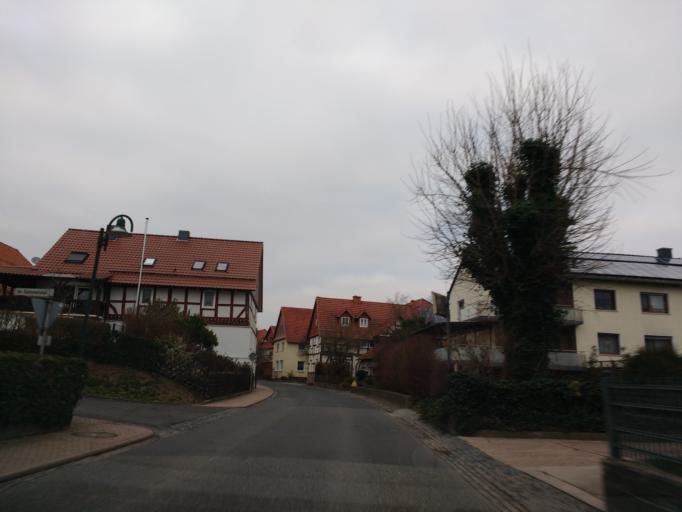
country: DE
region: Hesse
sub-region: Regierungsbezirk Kassel
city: Rotenburg an der Fulda
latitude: 51.0480
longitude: 9.7677
